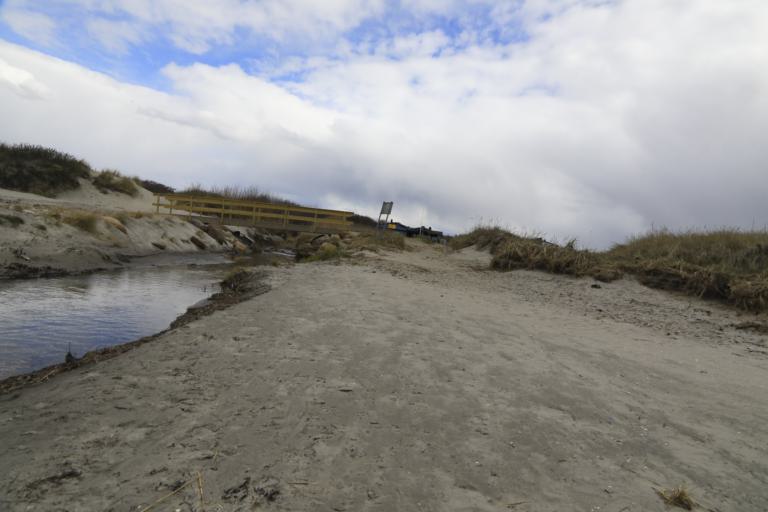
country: SE
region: Halland
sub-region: Varbergs Kommun
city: Traslovslage
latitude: 57.0795
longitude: 12.2612
